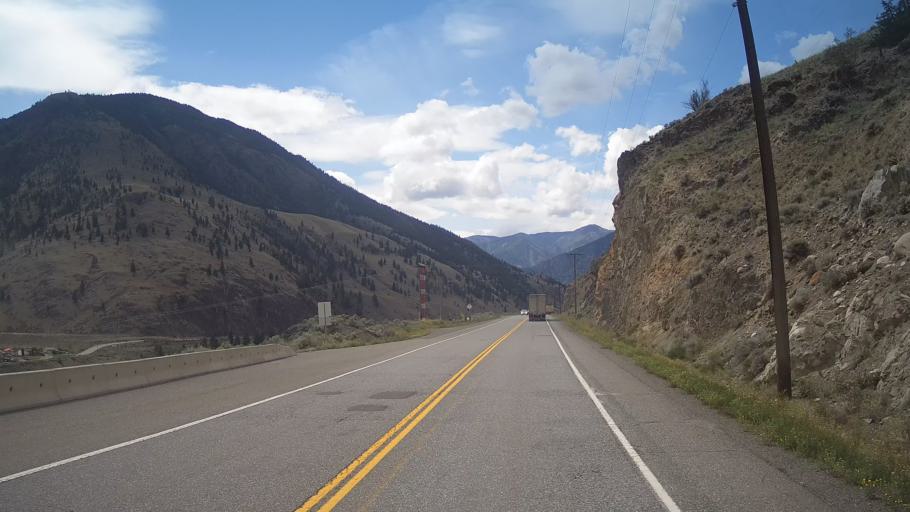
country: CA
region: British Columbia
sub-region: Thompson-Nicola Regional District
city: Ashcroft
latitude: 50.4308
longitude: -121.3154
